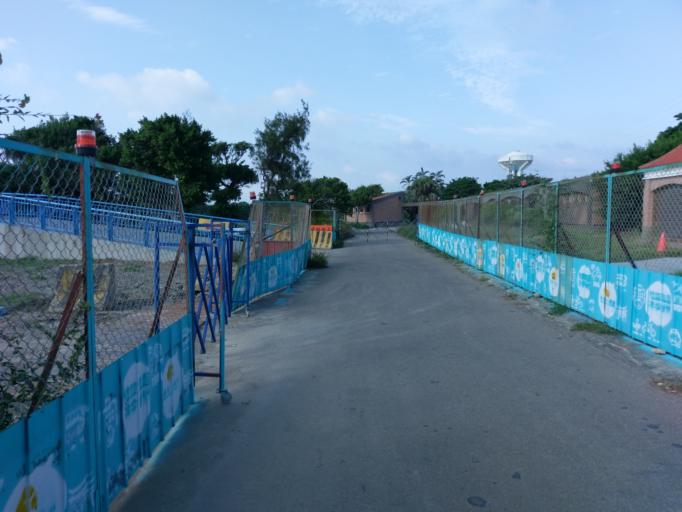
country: TW
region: Taiwan
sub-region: Hsinchu
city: Hsinchu
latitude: 24.8225
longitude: 120.9098
